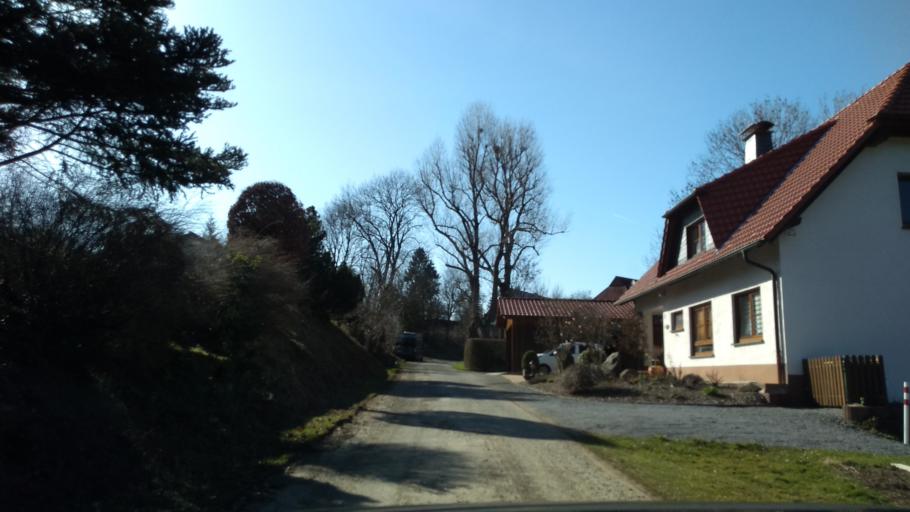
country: DE
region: North Rhine-Westphalia
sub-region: Regierungsbezirk Arnsberg
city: Herscheid
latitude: 51.1702
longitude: 7.7071
